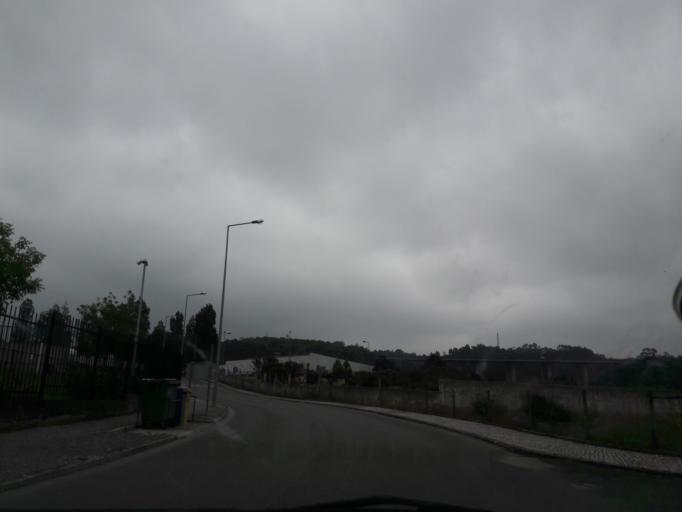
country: PT
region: Leiria
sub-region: Obidos
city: Obidos
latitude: 39.3530
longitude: -9.1607
